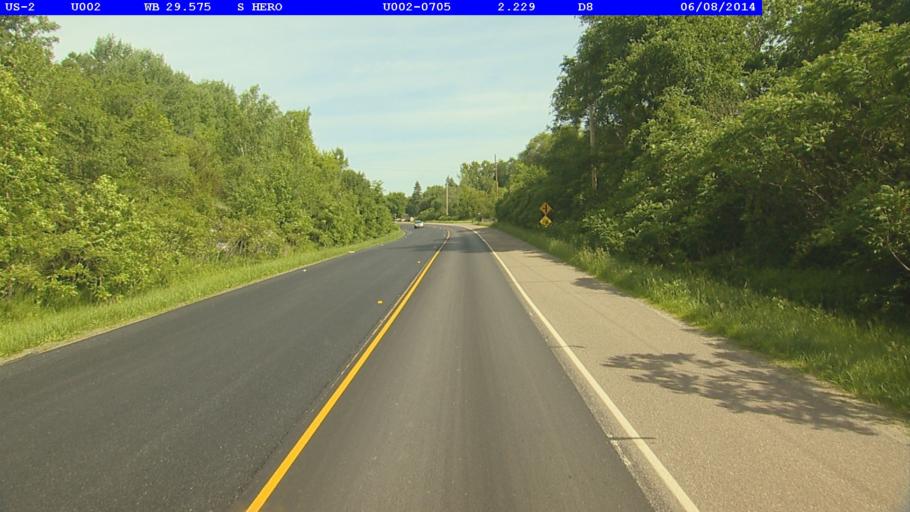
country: US
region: New York
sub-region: Clinton County
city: Cumberland Head
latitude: 44.6500
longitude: -73.3161
